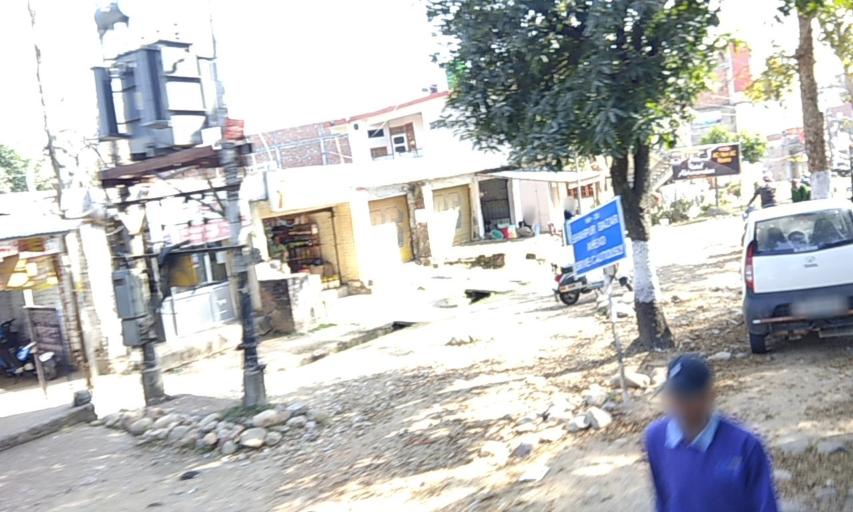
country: IN
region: Himachal Pradesh
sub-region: Kangra
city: Yol
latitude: 32.2157
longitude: 76.1804
